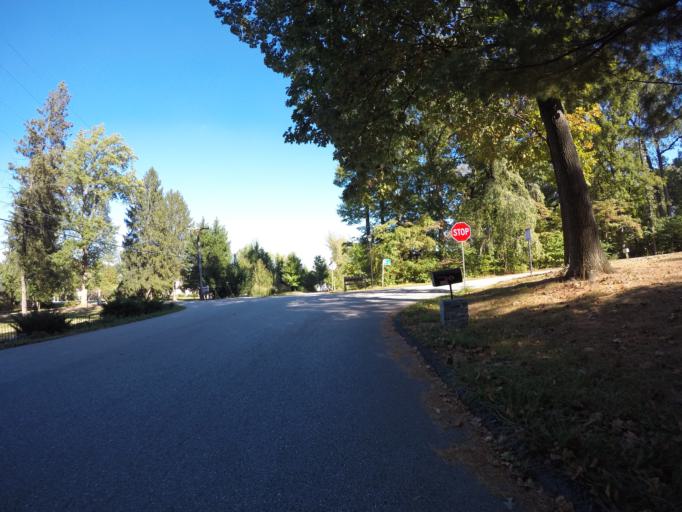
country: US
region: Maryland
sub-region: Howard County
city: Ellicott City
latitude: 39.2908
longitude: -76.8040
